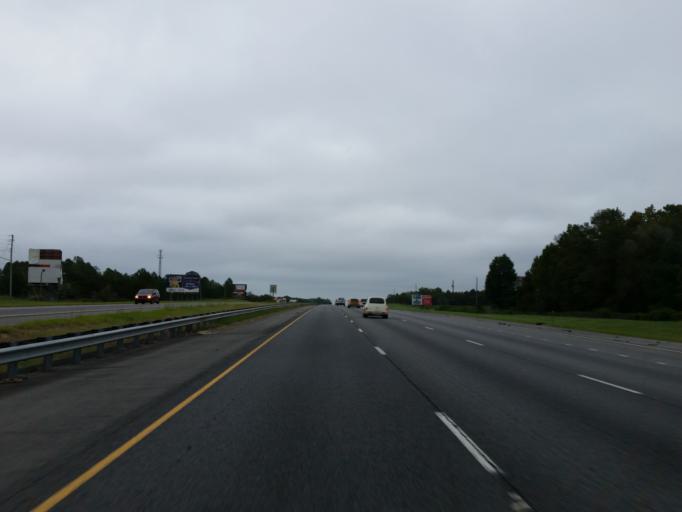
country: US
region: Georgia
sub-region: Crisp County
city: Cordele
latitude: 31.9024
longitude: -83.7359
